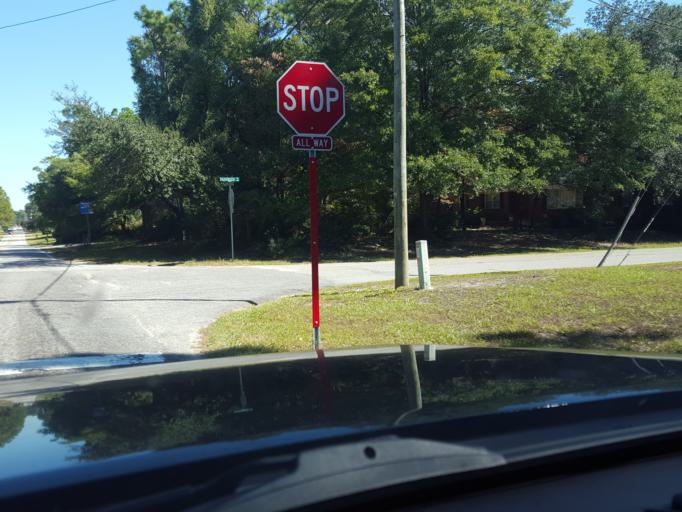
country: US
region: North Carolina
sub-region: New Hanover County
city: Seagate
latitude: 34.2023
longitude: -77.8864
